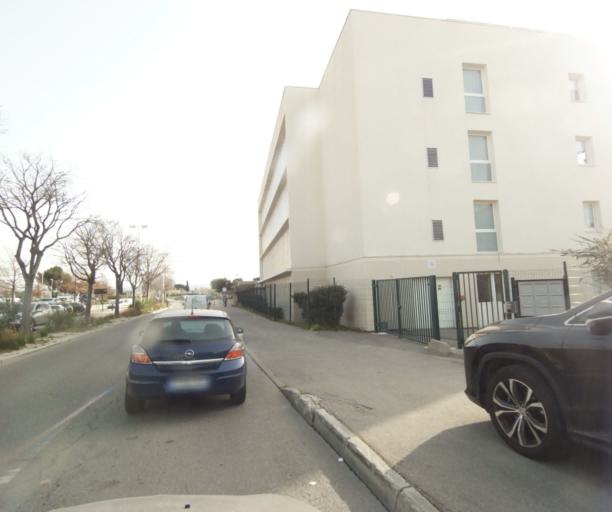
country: FR
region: Provence-Alpes-Cote d'Azur
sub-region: Departement des Bouches-du-Rhone
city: Vitrolles
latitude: 43.4478
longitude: 5.2470
